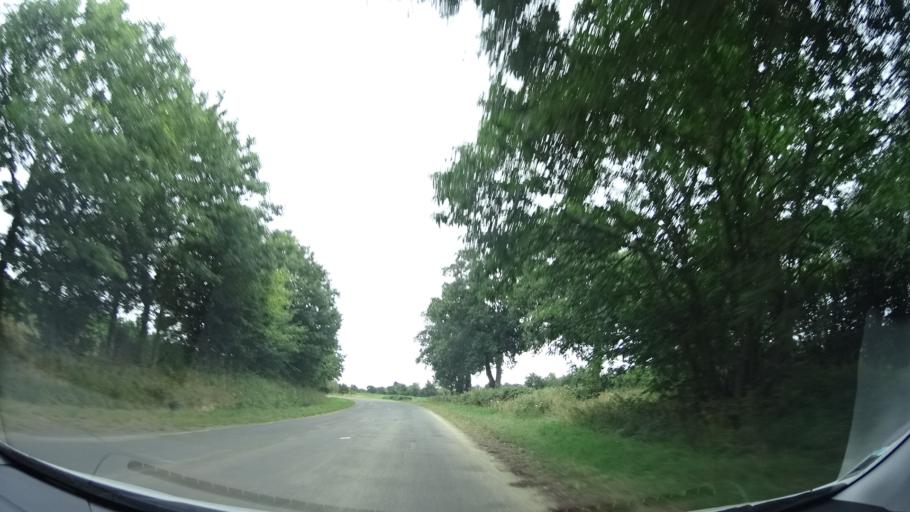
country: FR
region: Brittany
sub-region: Departement d'Ille-et-Vilaine
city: Vignoc
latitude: 48.2653
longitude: -1.7776
